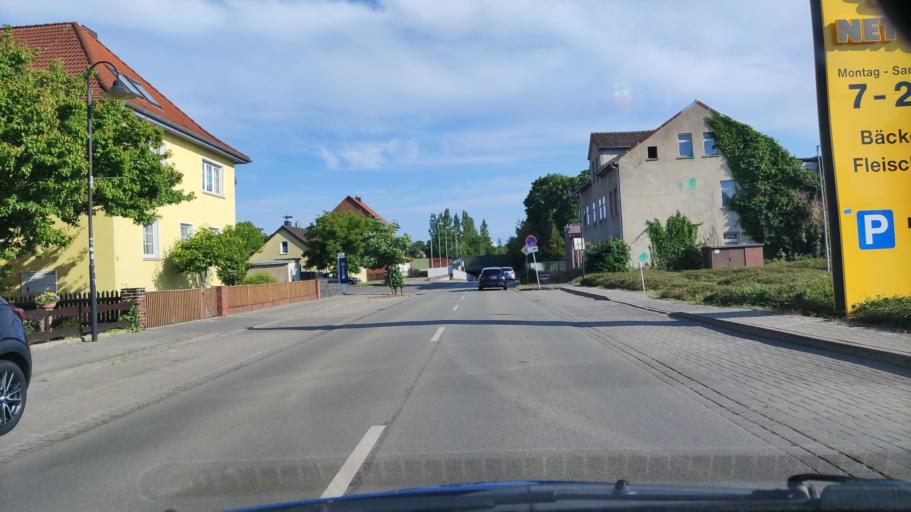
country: DE
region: Saxony-Anhalt
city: Gardelegen
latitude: 52.5189
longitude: 11.3974
